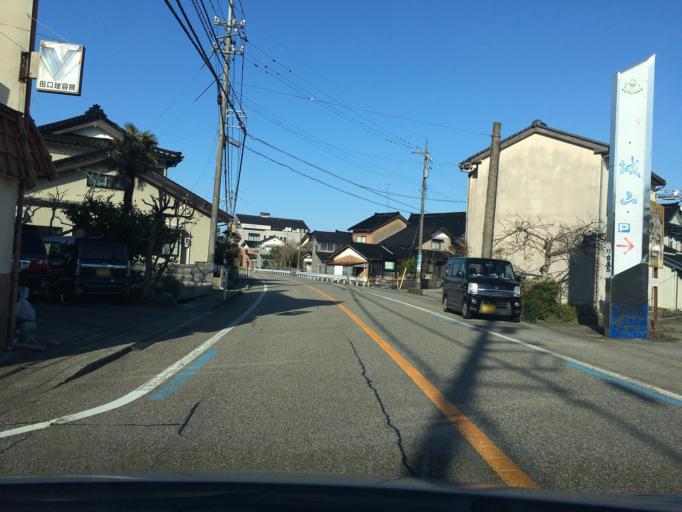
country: JP
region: Toyama
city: Himi
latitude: 36.8830
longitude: 136.9919
